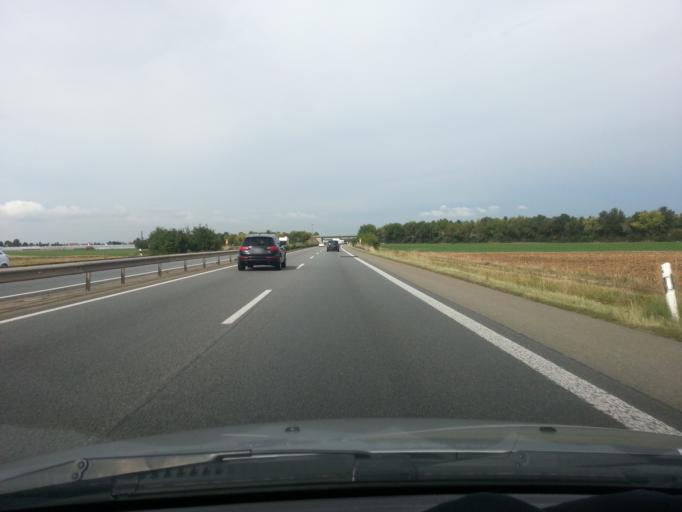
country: DE
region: Rheinland-Pfalz
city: Hochdorf-Assenheim
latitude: 49.4044
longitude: 8.2794
